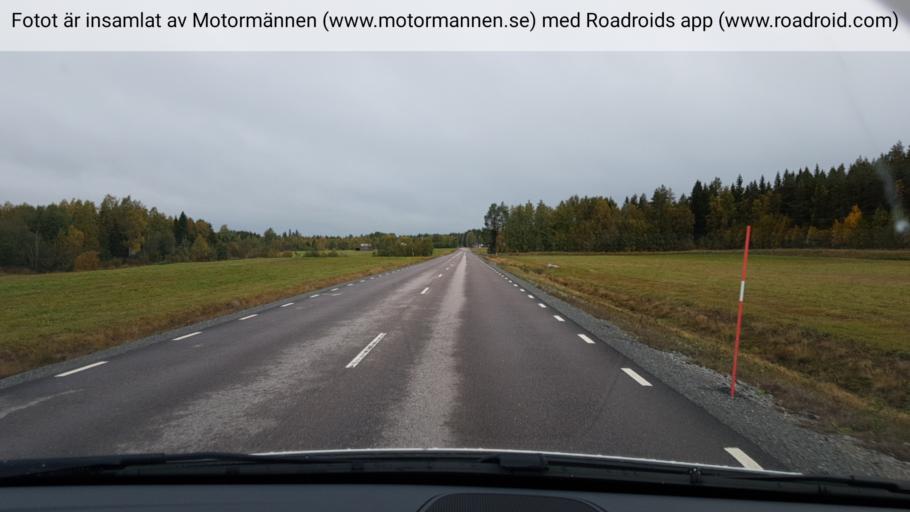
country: SE
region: Vaesterbotten
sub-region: Umea Kommun
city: Ersmark
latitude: 63.9107
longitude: 20.3109
